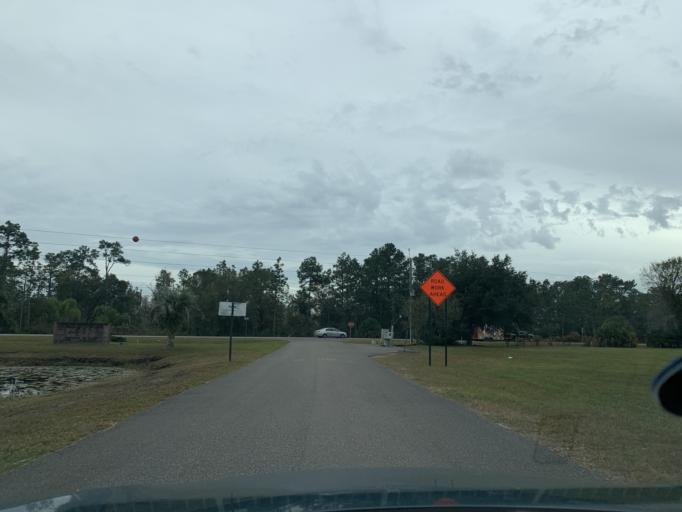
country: US
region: Florida
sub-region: Pasco County
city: Shady Hills
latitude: 28.3246
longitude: -82.4960
